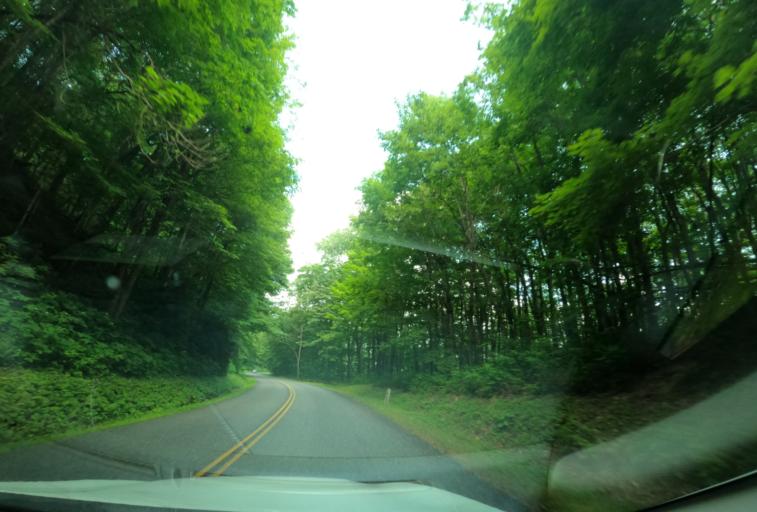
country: US
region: North Carolina
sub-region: Haywood County
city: Hazelwood
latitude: 35.4386
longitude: -83.0493
